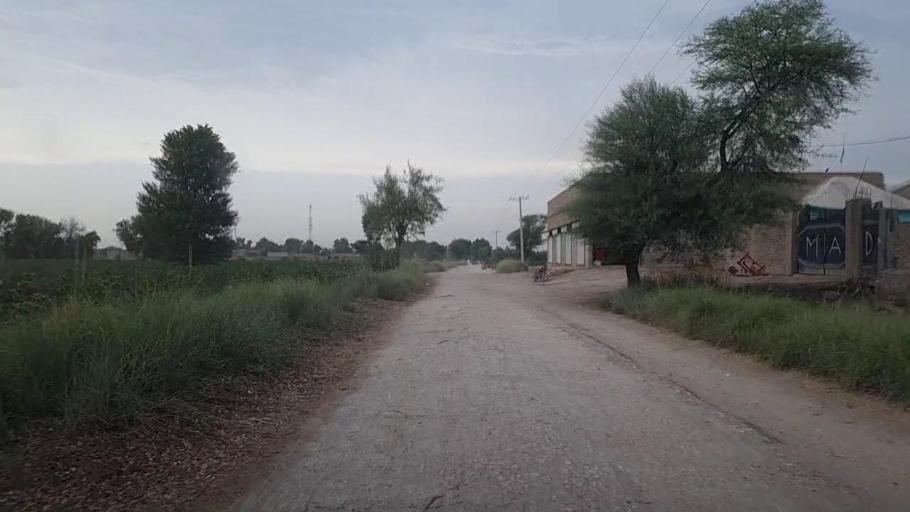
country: PK
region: Sindh
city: Karaundi
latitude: 26.9813
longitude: 68.3438
